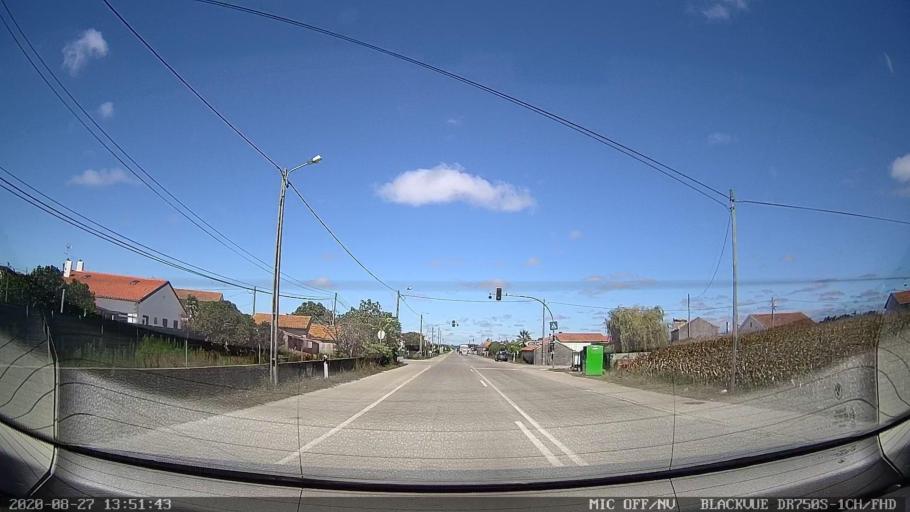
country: PT
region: Coimbra
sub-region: Mira
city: Mira
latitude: 40.3452
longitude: -8.7493
